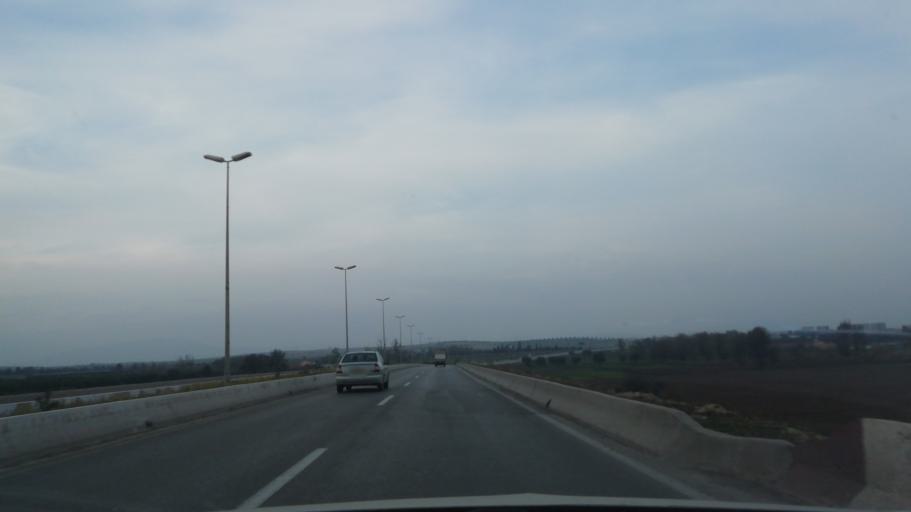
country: DZ
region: Sidi Bel Abbes
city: Sidi Bel Abbes
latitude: 35.1868
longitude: -0.6601
